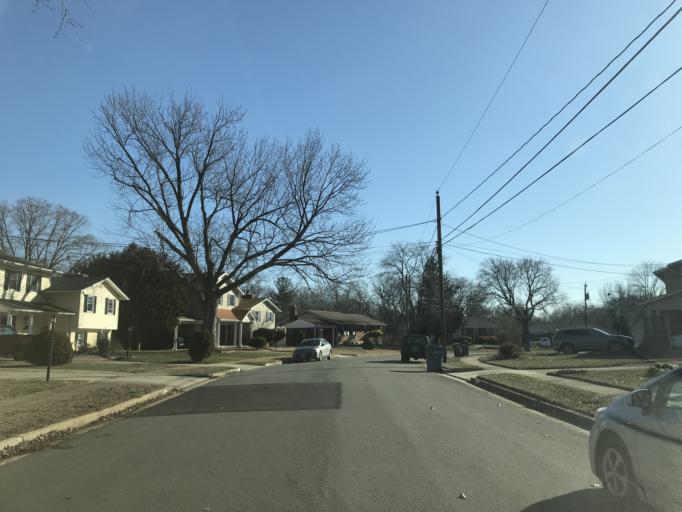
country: US
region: Virginia
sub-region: Fairfax County
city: Springfield
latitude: 38.7858
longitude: -77.1699
